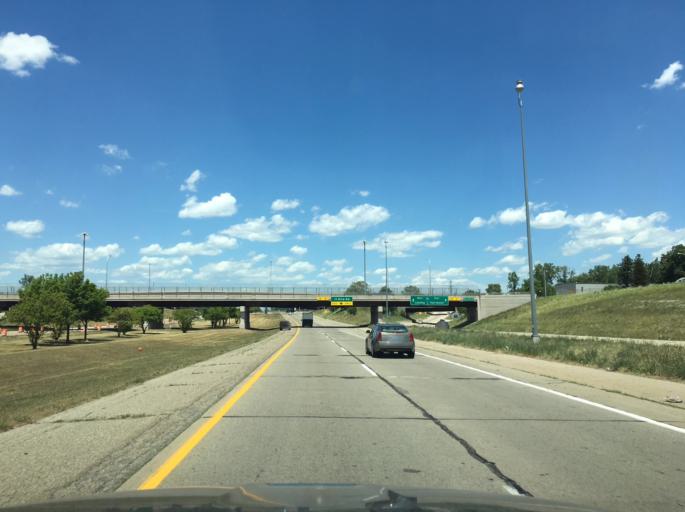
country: US
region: Michigan
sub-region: Macomb County
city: Center Line
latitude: 42.4831
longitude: -83.0454
